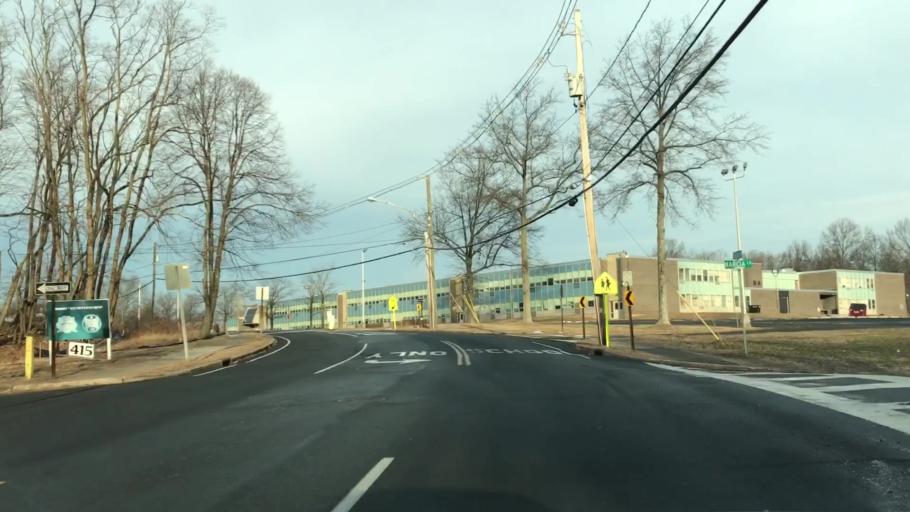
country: US
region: New York
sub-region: Rockland County
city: Kaser
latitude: 41.1346
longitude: -74.0608
